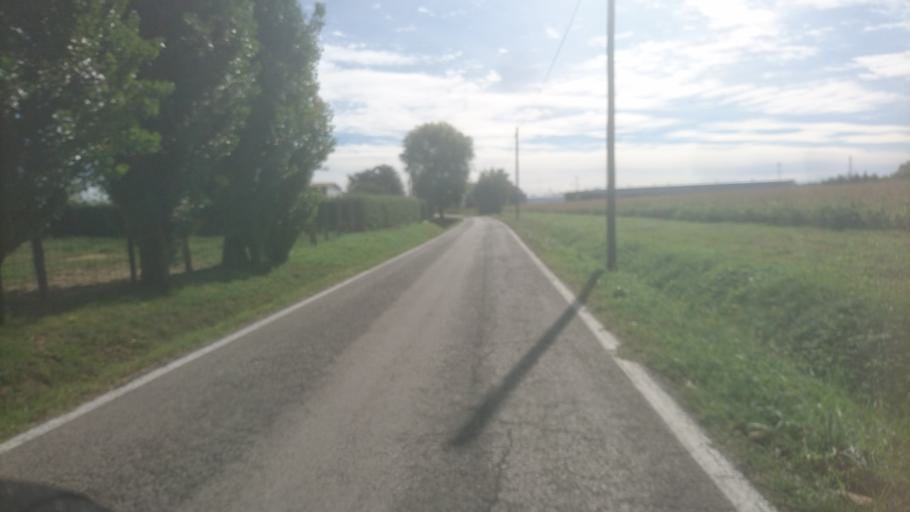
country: IT
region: Veneto
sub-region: Provincia di Vicenza
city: Montegalda
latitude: 45.4620
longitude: 11.6901
